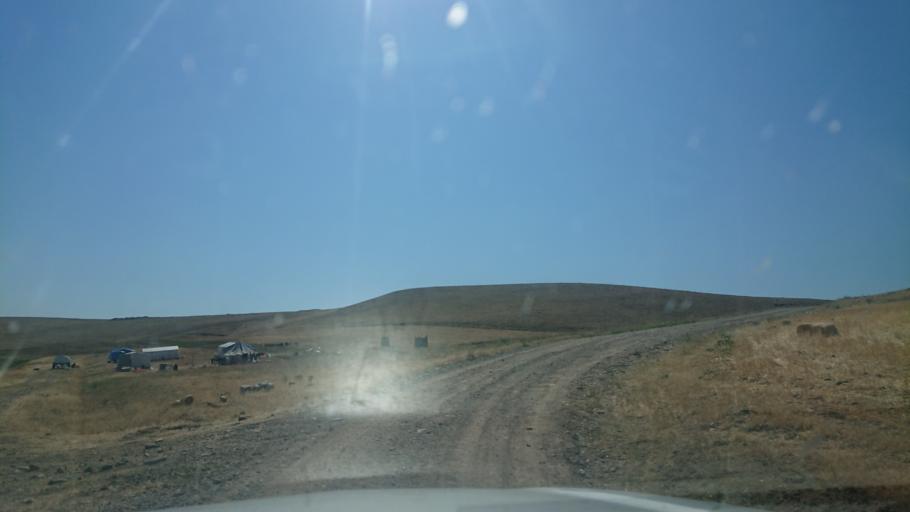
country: TR
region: Aksaray
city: Sariyahsi
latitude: 39.0558
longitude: 33.8839
